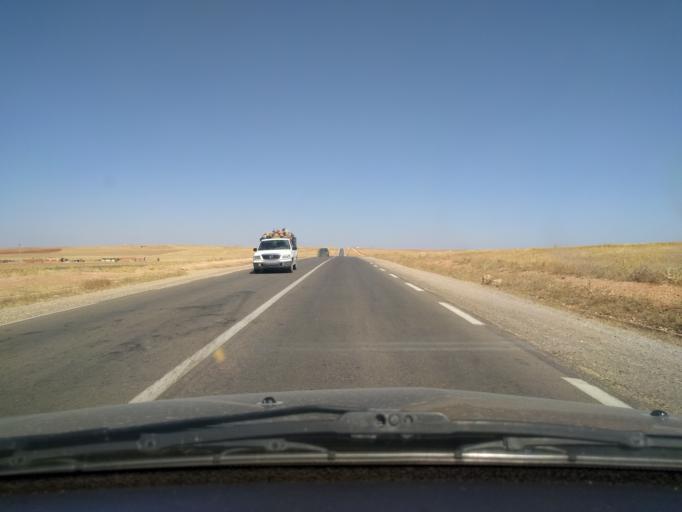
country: DZ
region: Tiaret
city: Frenda
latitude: 34.8848
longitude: 1.1876
